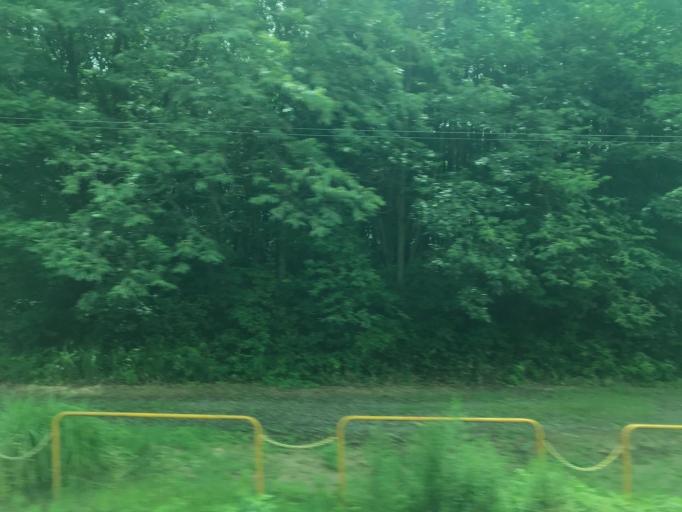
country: JP
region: Tochigi
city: Kuroiso
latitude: 36.9923
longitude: 140.0857
